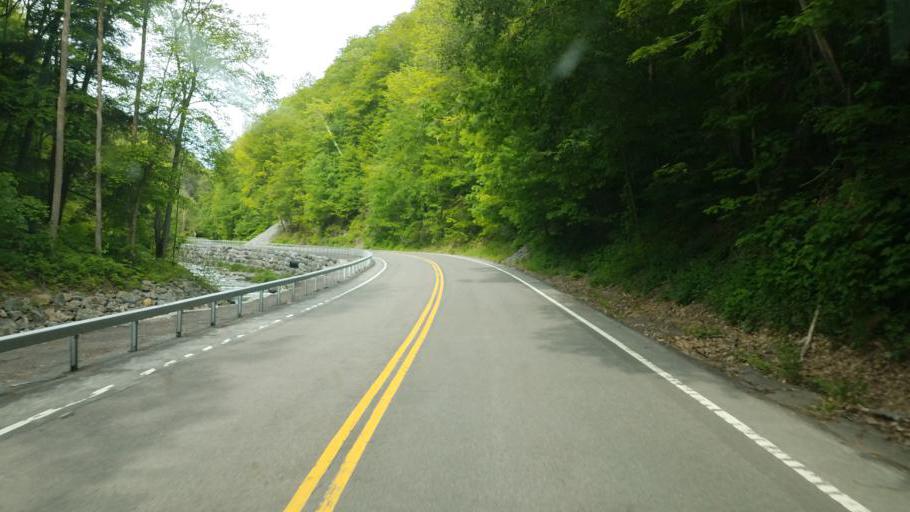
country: US
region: New York
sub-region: Herkimer County
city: Ilion
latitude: 42.9894
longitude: -75.0691
